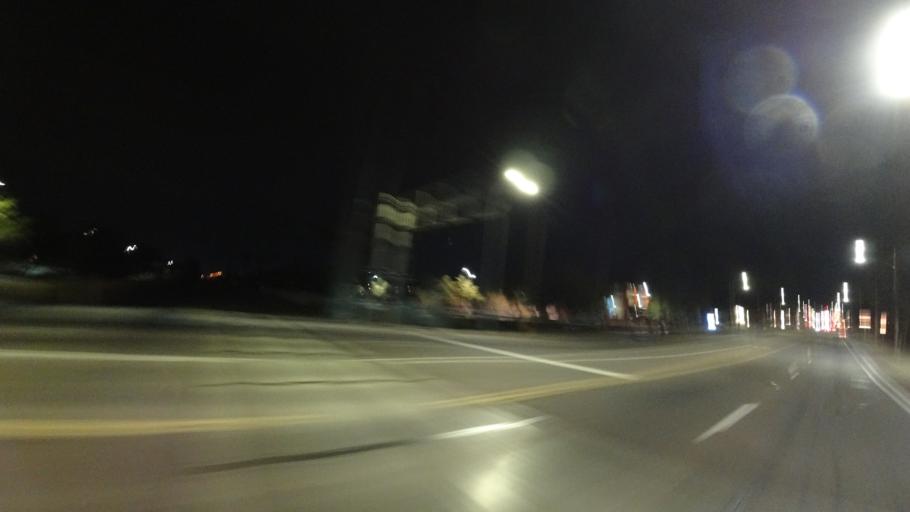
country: US
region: Arizona
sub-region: Maricopa County
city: Chandler
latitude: 33.3061
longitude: -111.8372
